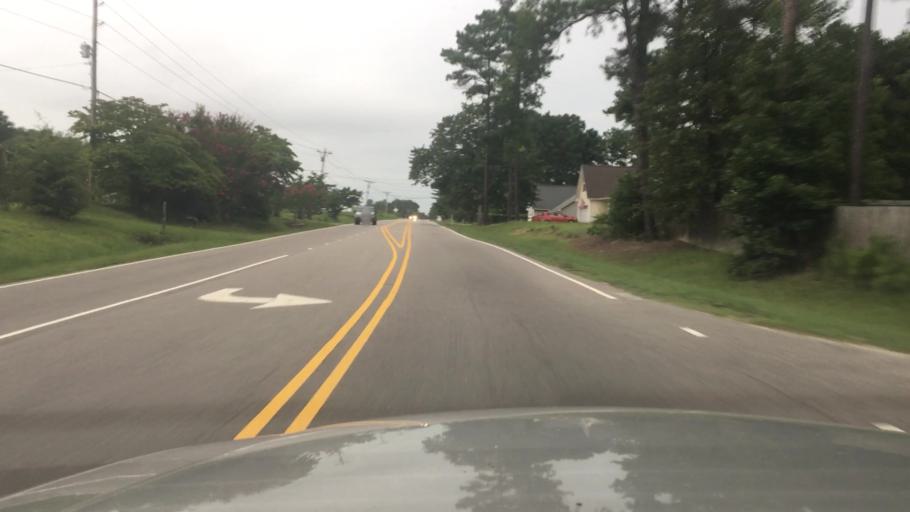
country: US
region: North Carolina
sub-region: Hoke County
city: Rockfish
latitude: 34.9682
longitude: -79.0529
